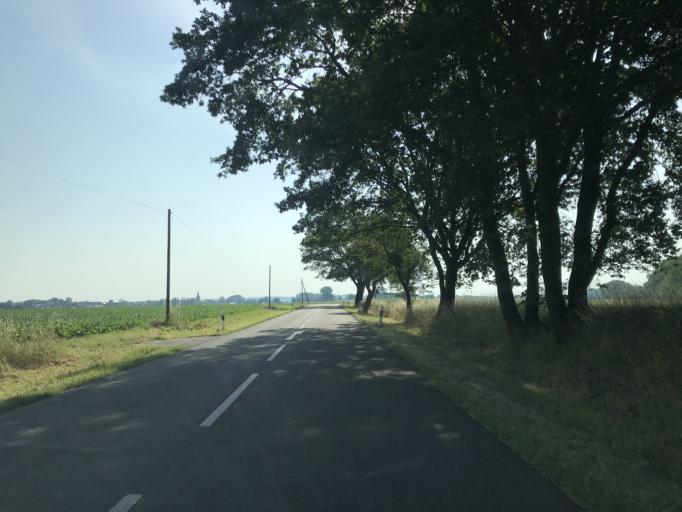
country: DE
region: Saxony-Anhalt
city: Erxleben
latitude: 52.2490
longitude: 11.2056
